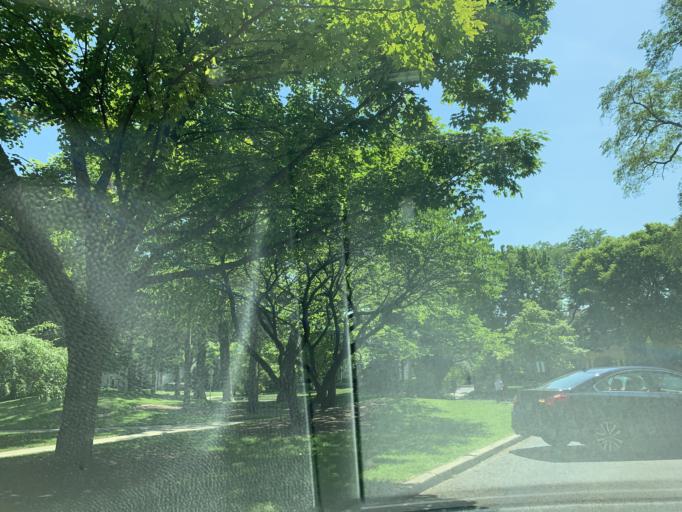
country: US
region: Illinois
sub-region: Cook County
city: Kenilworth
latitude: 42.0981
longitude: -87.7157
